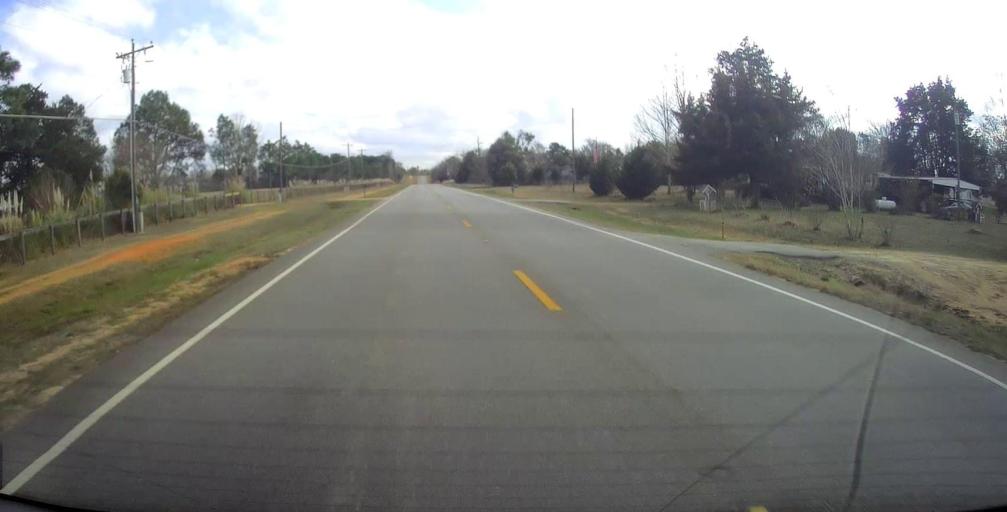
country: US
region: Georgia
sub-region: Marion County
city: Buena Vista
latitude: 32.4594
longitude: -84.5380
